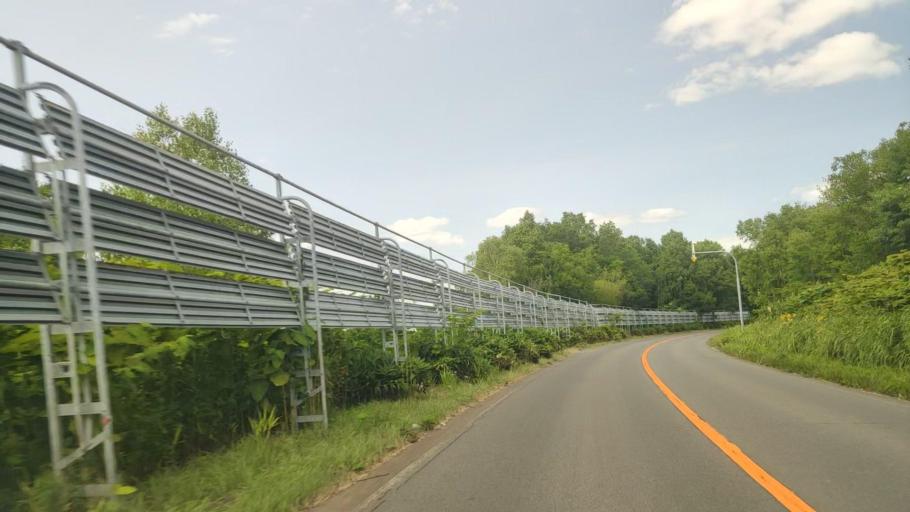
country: JP
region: Hokkaido
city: Nayoro
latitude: 44.2482
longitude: 142.4157
